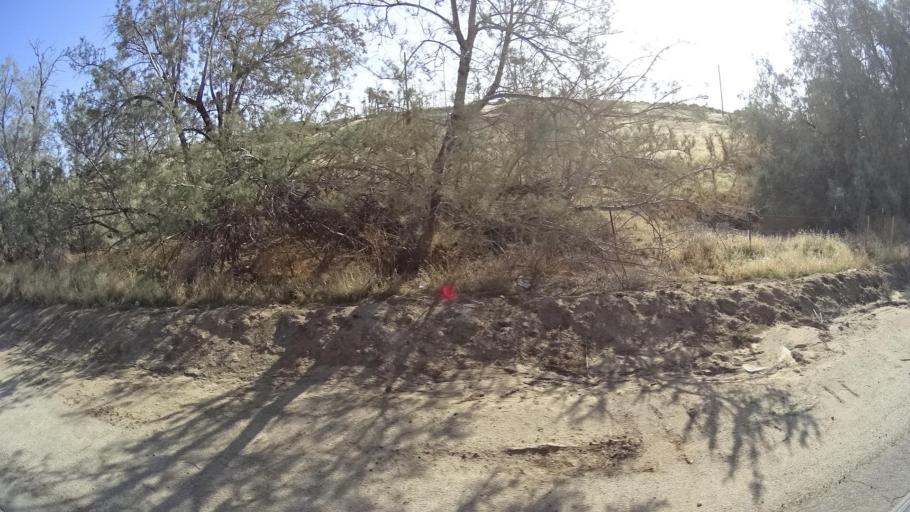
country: US
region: California
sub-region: Kern County
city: Oildale
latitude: 35.4975
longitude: -119.0393
